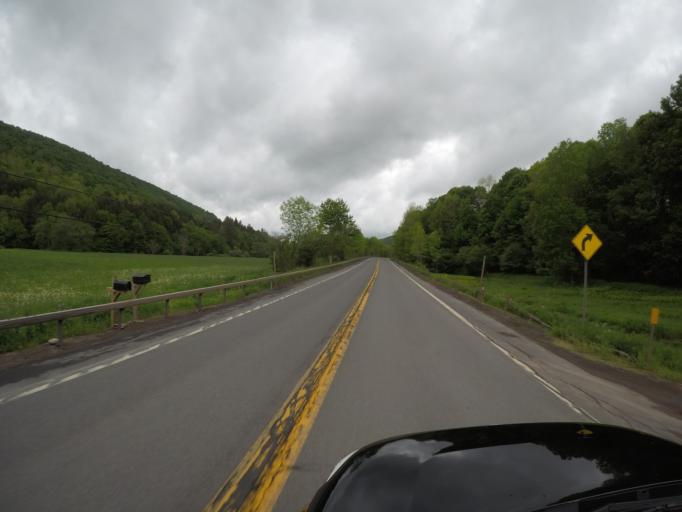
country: US
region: New York
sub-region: Delaware County
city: Delhi
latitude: 42.2558
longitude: -74.8576
